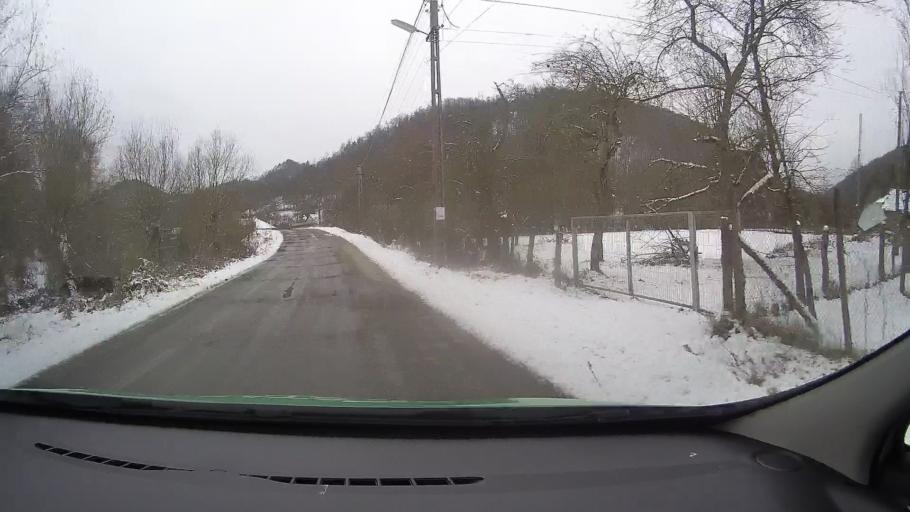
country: RO
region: Hunedoara
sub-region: Comuna Balsa
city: Balsa
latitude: 46.0557
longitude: 23.0821
